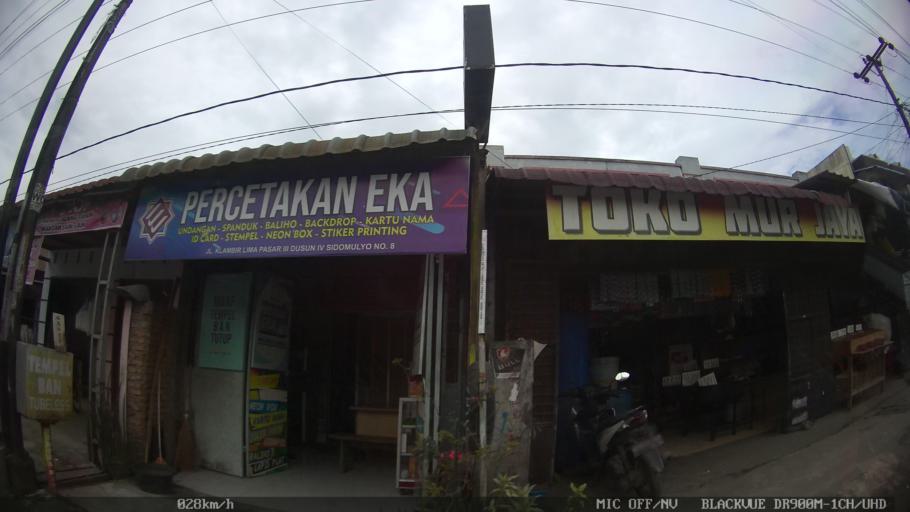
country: ID
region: North Sumatra
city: Sunggal
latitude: 3.6413
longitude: 98.5940
